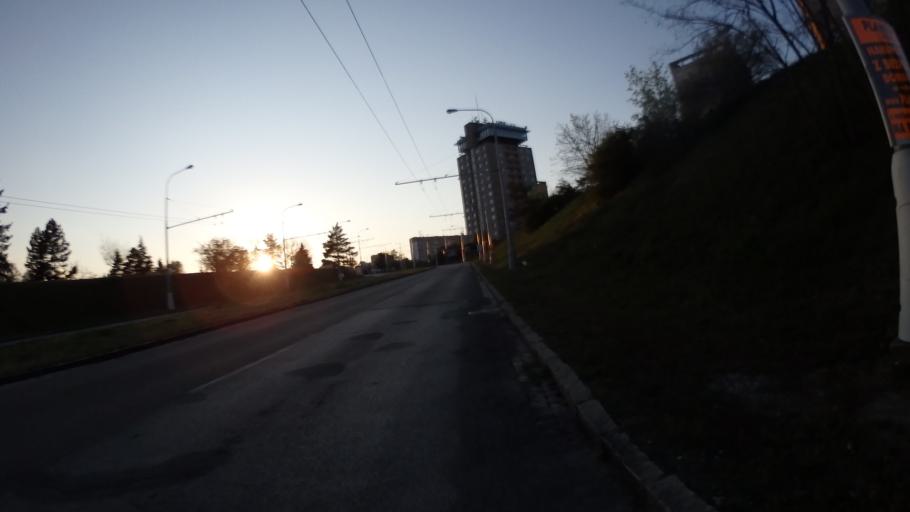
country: CZ
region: South Moravian
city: Ostopovice
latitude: 49.1960
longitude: 16.5369
